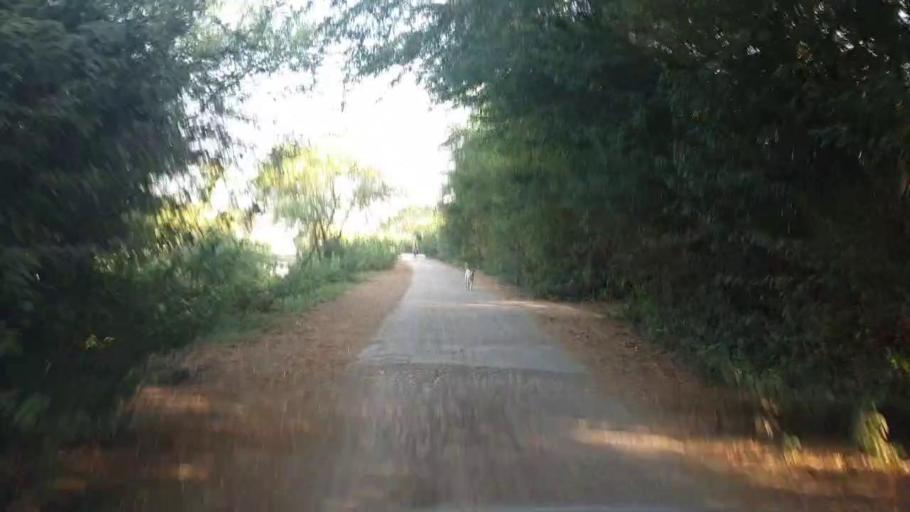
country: PK
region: Sindh
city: Badin
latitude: 24.6877
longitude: 68.8163
